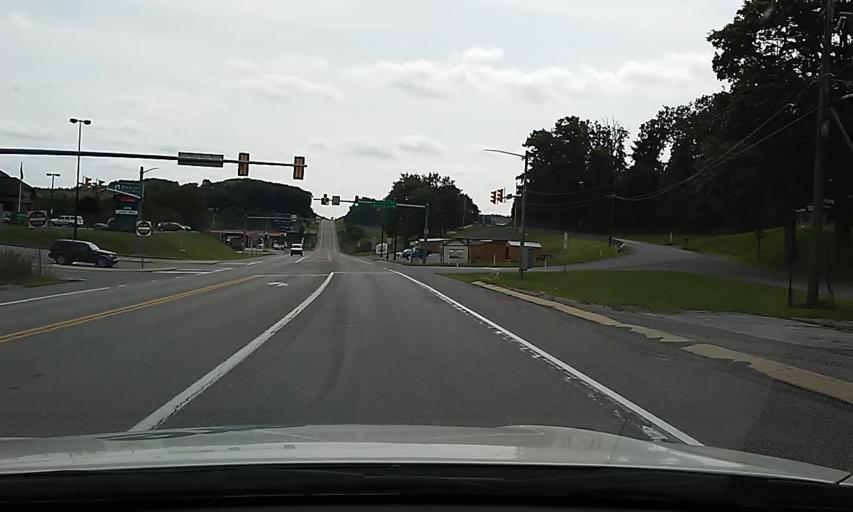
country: US
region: Pennsylvania
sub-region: Jefferson County
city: Punxsutawney
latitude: 40.9281
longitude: -78.9837
